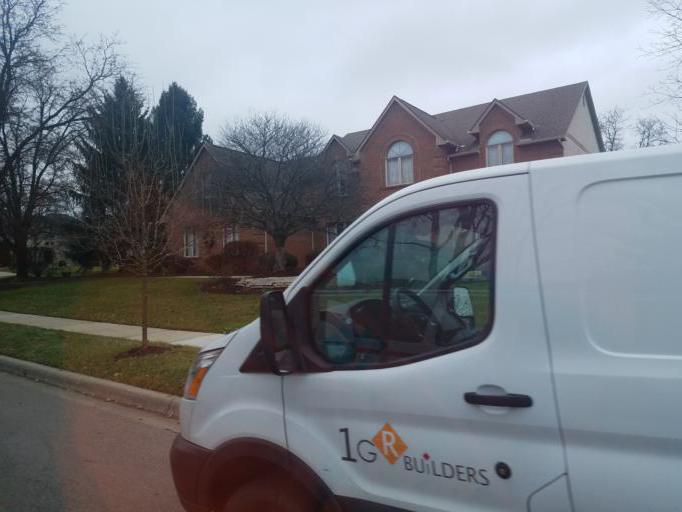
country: US
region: Ohio
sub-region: Franklin County
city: Westerville
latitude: 40.1342
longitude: -82.9567
